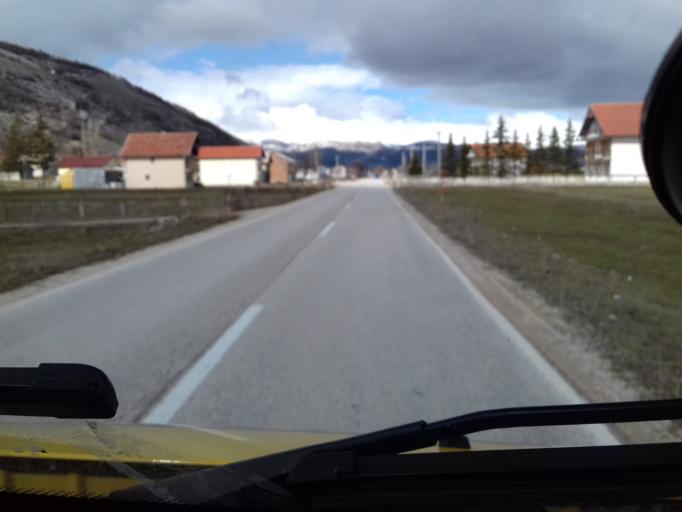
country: BA
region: Federation of Bosnia and Herzegovina
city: Tomislavgrad
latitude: 43.6582
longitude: 17.2131
